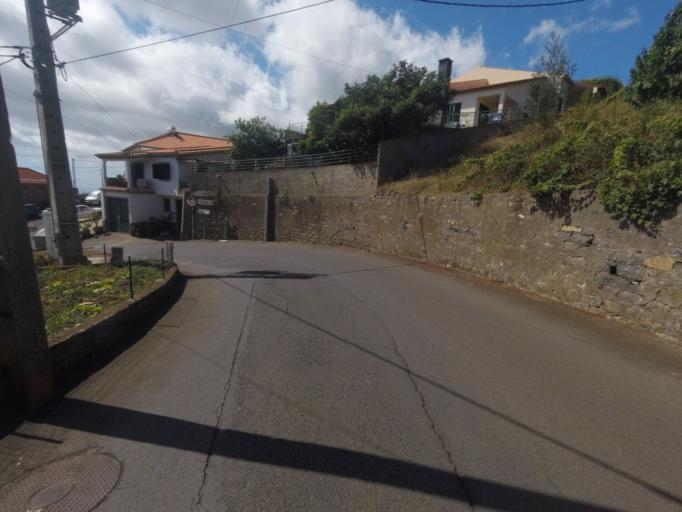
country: PT
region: Madeira
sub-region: Ribeira Brava
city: Campanario
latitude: 32.6809
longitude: -17.0436
